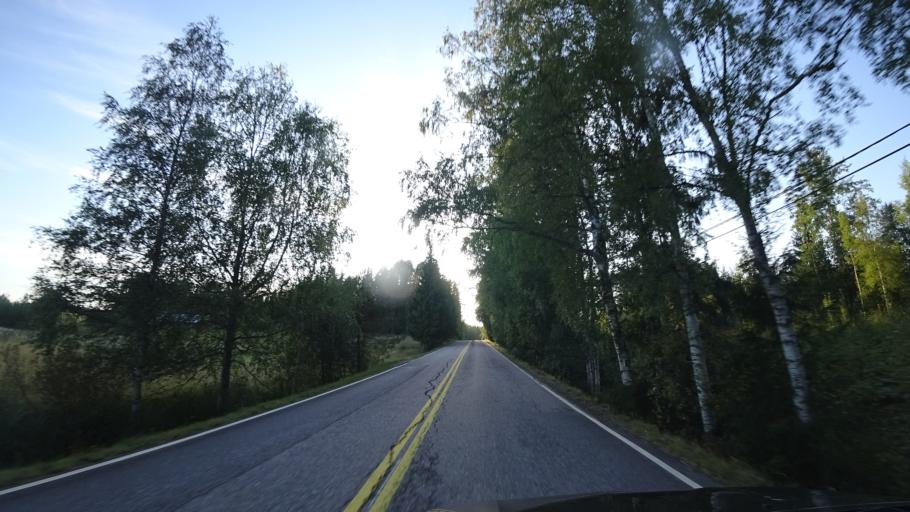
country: FI
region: Haeme
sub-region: Haemeenlinna
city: Tuulos
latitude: 61.0068
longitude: 24.8698
